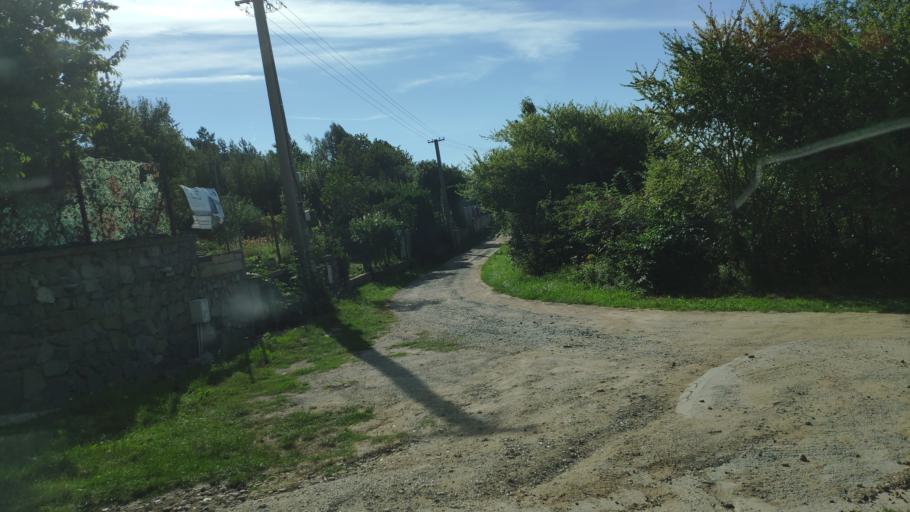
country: SK
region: Kosicky
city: Kosice
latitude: 48.7661
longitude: 21.2507
